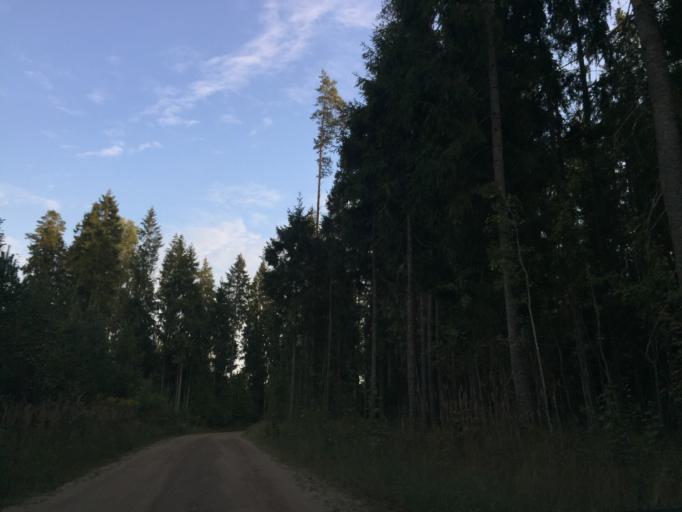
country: LV
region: Baldone
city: Baldone
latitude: 56.7662
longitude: 24.4066
